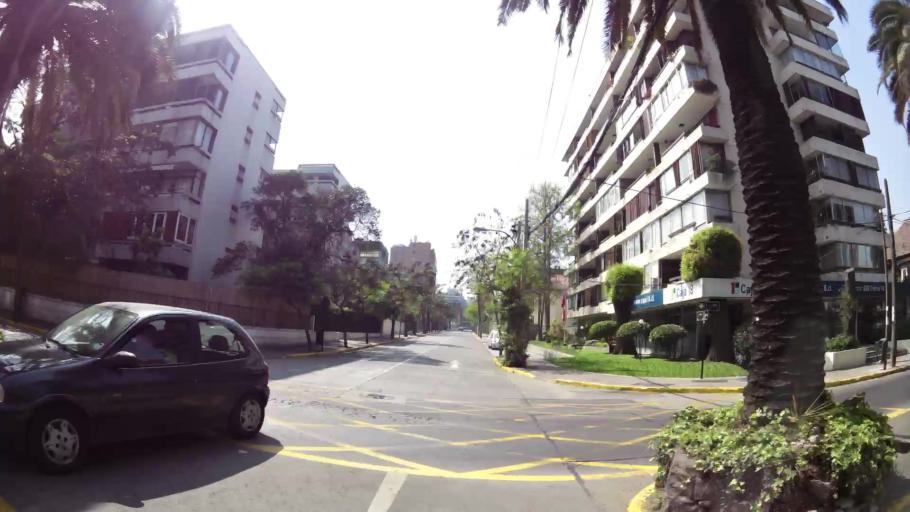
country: CL
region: Santiago Metropolitan
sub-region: Provincia de Santiago
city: Villa Presidente Frei, Nunoa, Santiago, Chile
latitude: -33.4228
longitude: -70.6070
